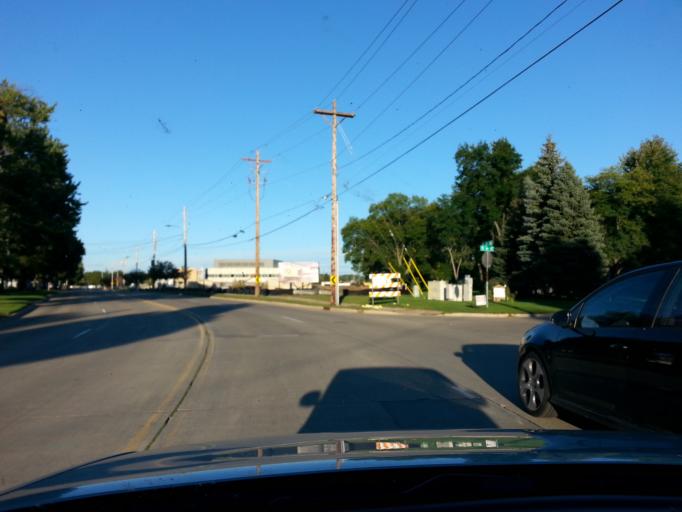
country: US
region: Minnesota
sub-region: Olmsted County
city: Rochester
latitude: 44.0193
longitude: -92.4438
